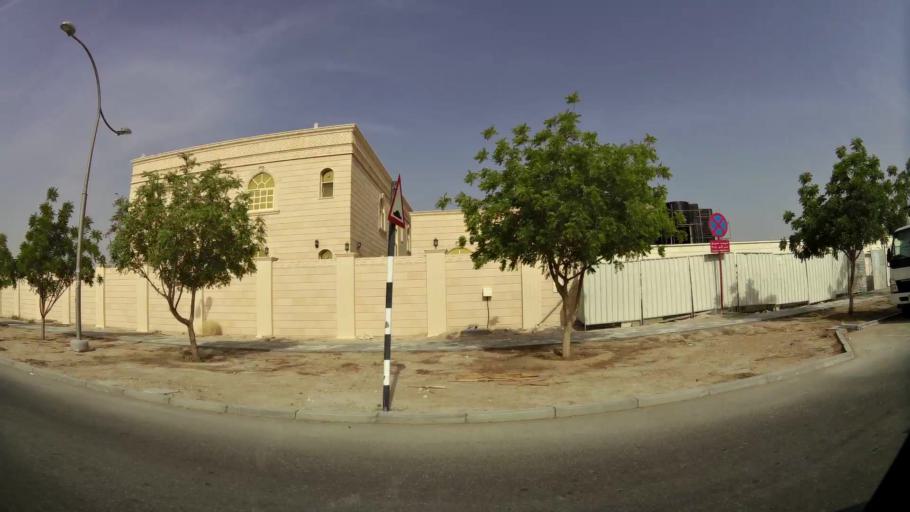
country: AE
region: Abu Dhabi
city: Al Ain
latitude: 24.1404
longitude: 55.7233
